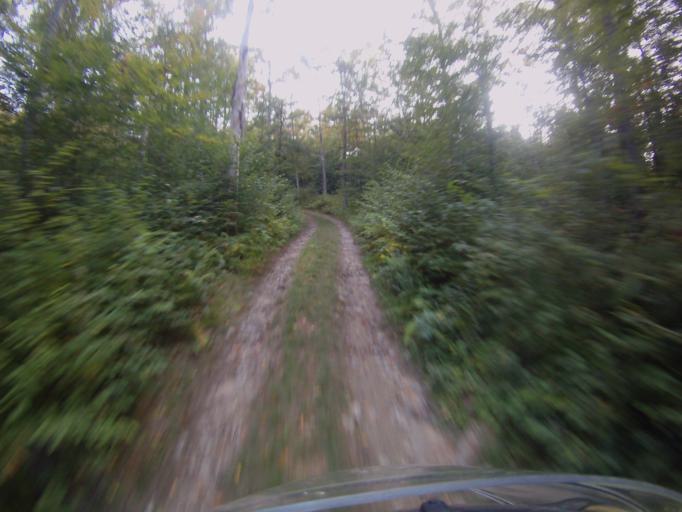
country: US
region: Vermont
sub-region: Addison County
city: Bristol
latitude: 44.0096
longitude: -73.0015
